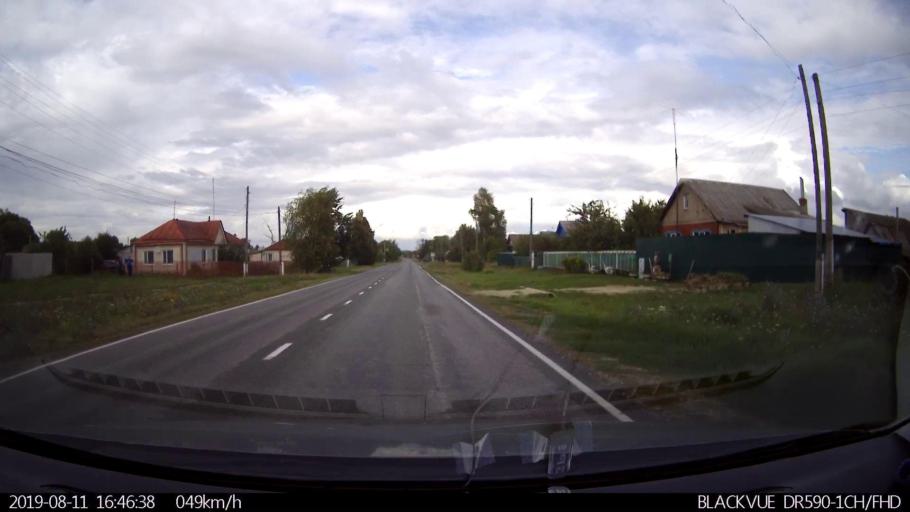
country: RU
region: Ulyanovsk
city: Mayna
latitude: 54.1989
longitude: 47.6902
